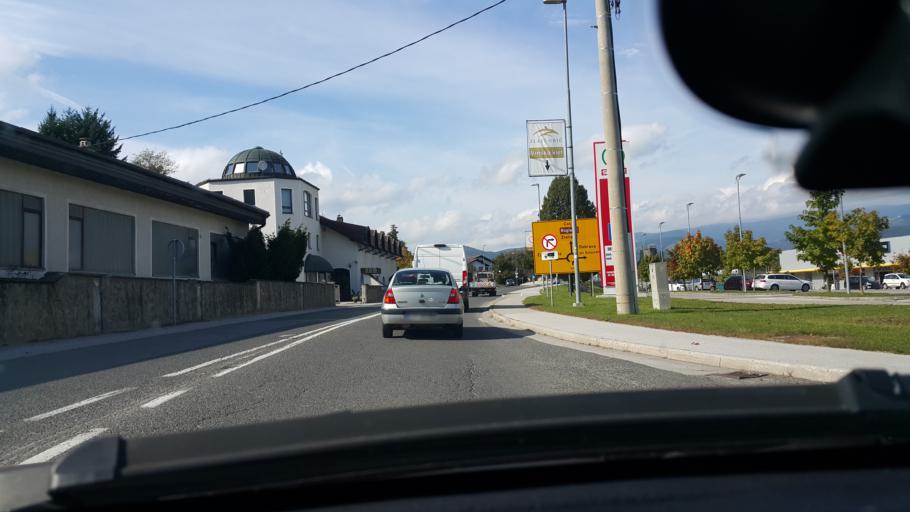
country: SI
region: Slovenska Konjice
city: Slovenske Konjice
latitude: 46.3409
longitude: 15.4159
